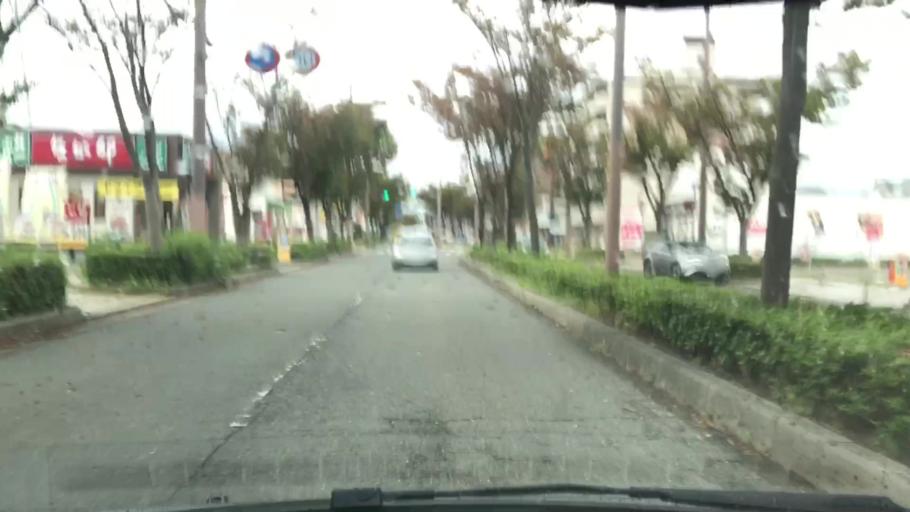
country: JP
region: Hyogo
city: Amagasaki
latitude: 34.7448
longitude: 135.3893
